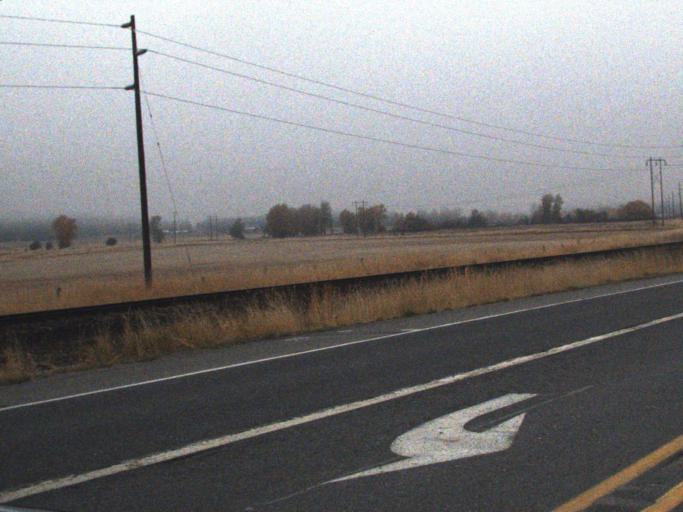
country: US
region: Washington
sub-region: Stevens County
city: Colville
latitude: 48.5670
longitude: -117.9367
